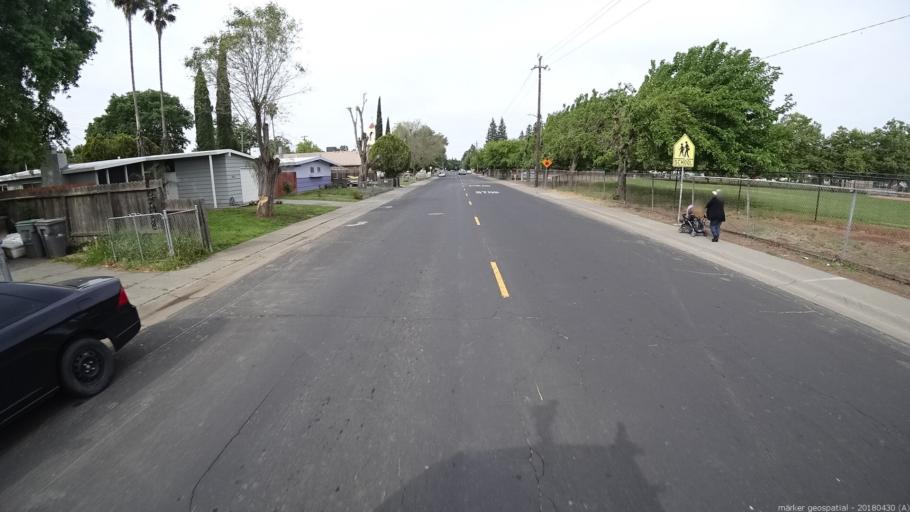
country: US
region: California
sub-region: Yolo County
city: West Sacramento
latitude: 38.5956
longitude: -121.5324
